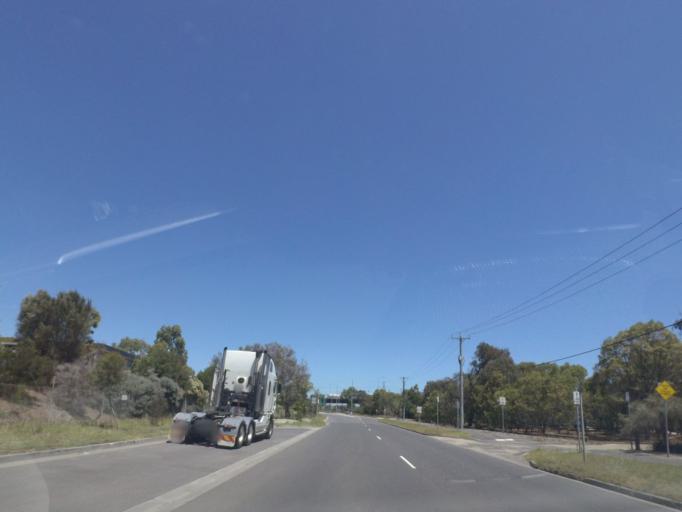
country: AU
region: Victoria
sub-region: Maribyrnong
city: Yarraville
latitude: -37.8305
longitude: 144.9118
